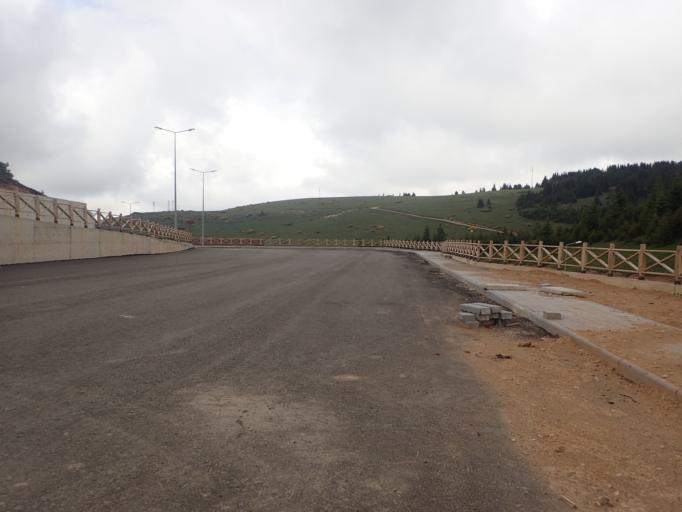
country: TR
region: Ordu
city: Topcam
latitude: 40.6361
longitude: 37.9399
